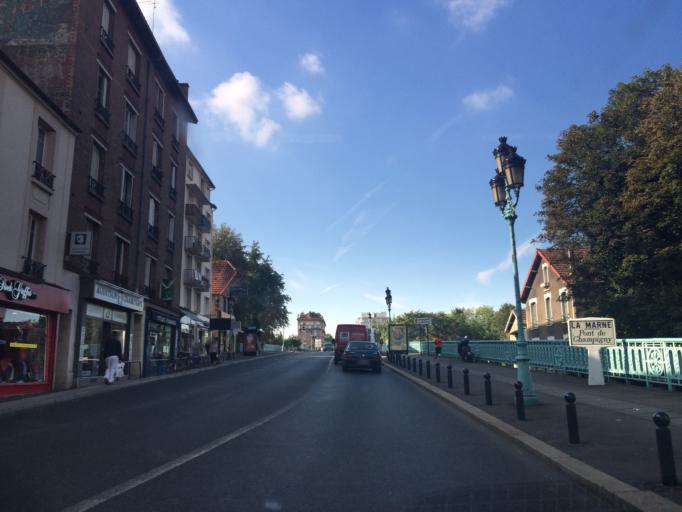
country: FR
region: Ile-de-France
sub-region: Departement du Val-de-Marne
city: Champigny-sur-Marne
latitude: 48.8115
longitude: 2.5104
